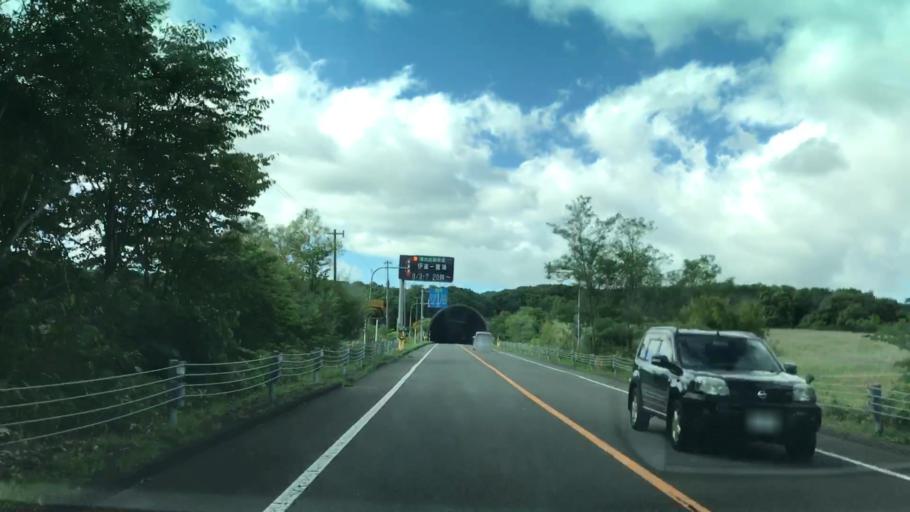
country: JP
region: Hokkaido
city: Muroran
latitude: 42.3815
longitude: 140.9646
